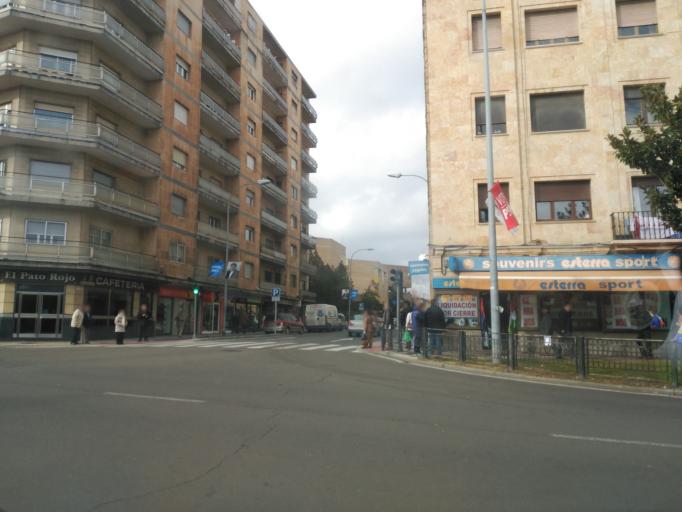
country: ES
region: Castille and Leon
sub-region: Provincia de Salamanca
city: Salamanca
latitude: 40.9665
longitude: -5.6699
